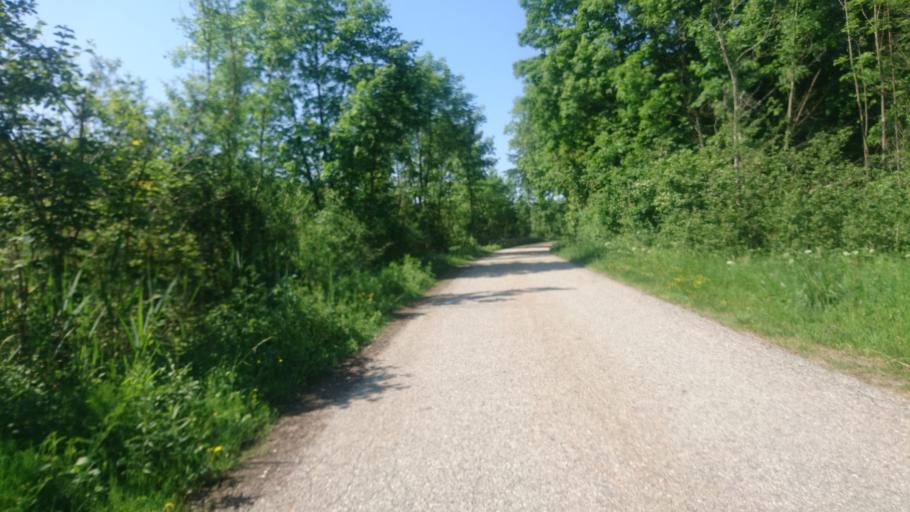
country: DE
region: Bavaria
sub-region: Upper Bavaria
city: Grunwald
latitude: 48.0497
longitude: 11.5214
